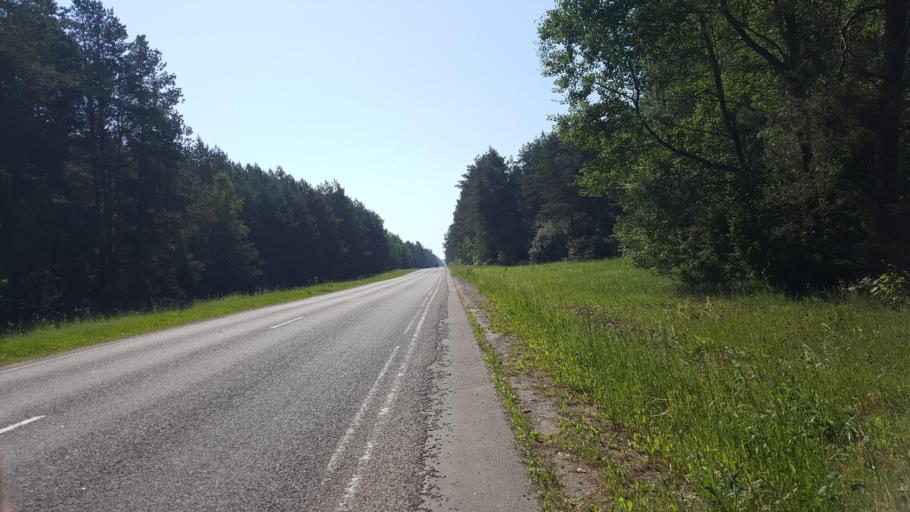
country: BY
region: Brest
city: Kamyanyets
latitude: 52.3814
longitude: 23.8636
